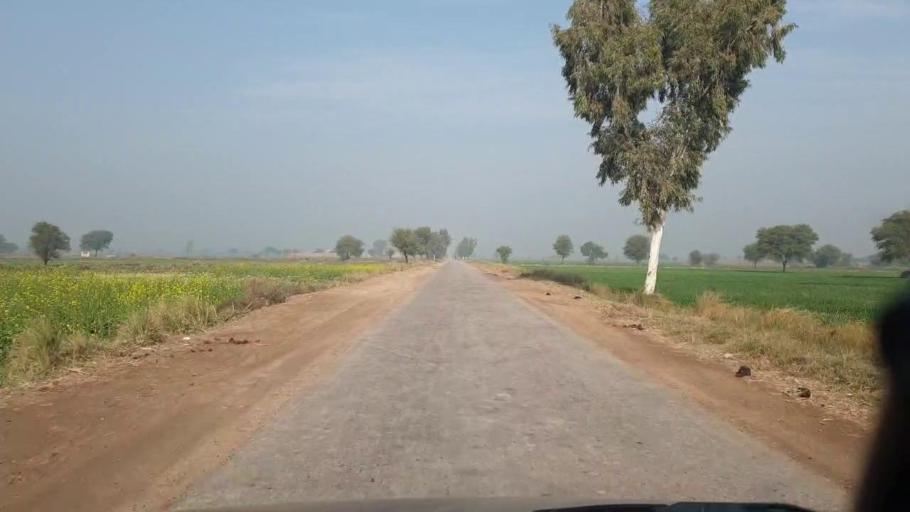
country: PK
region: Sindh
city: Shahdadpur
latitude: 25.9758
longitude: 68.5753
